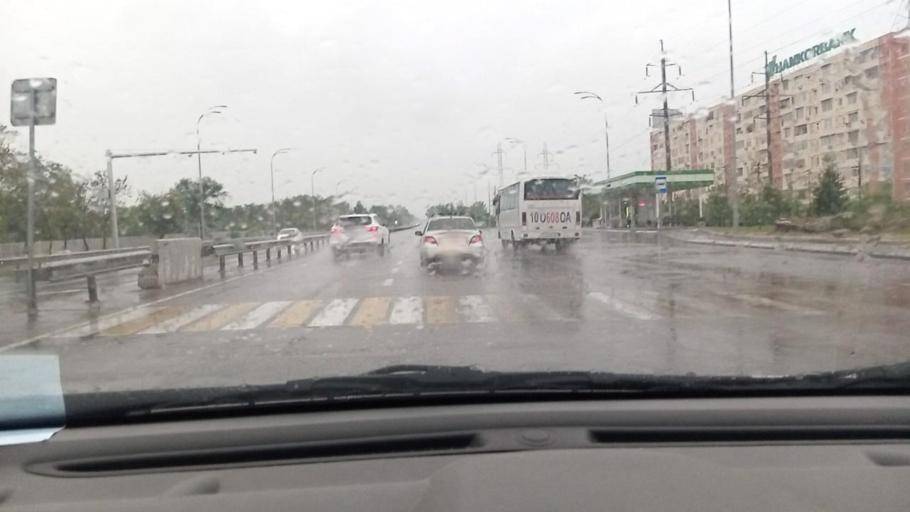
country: UZ
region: Toshkent Shahri
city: Bektemir
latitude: 41.2577
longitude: 69.3794
